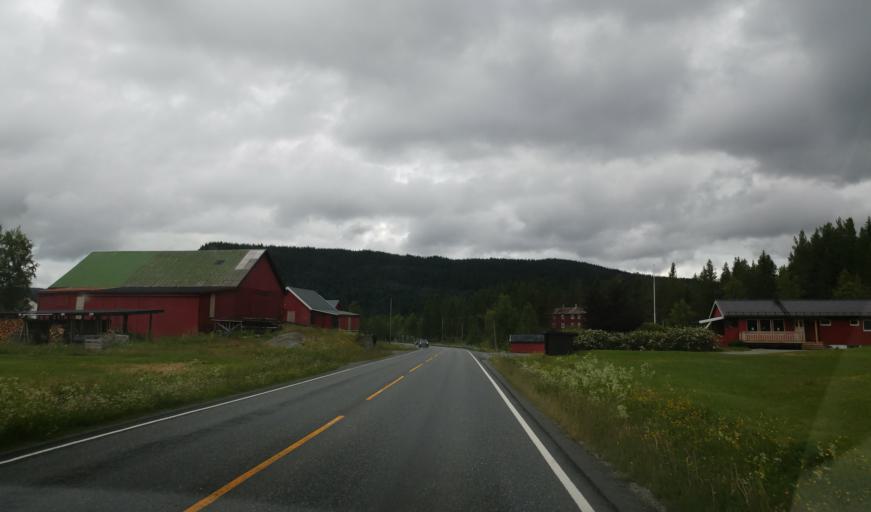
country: NO
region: Sor-Trondelag
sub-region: Selbu
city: Mebonden
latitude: 63.3783
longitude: 11.0807
